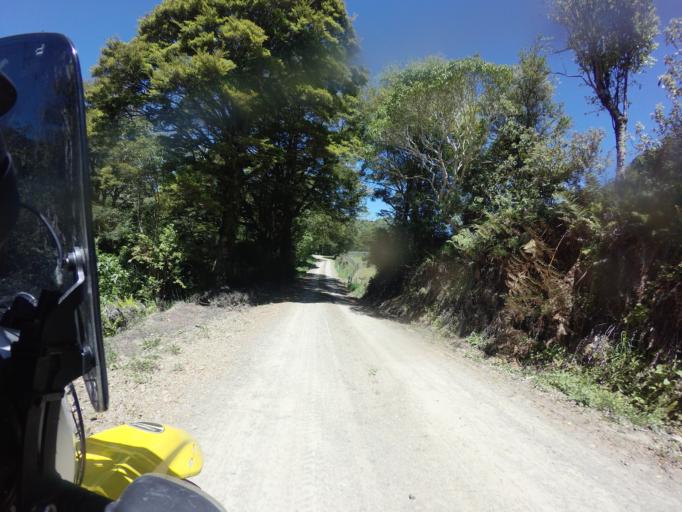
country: NZ
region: Bay of Plenty
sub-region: Opotiki District
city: Opotiki
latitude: -38.4130
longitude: 177.4088
